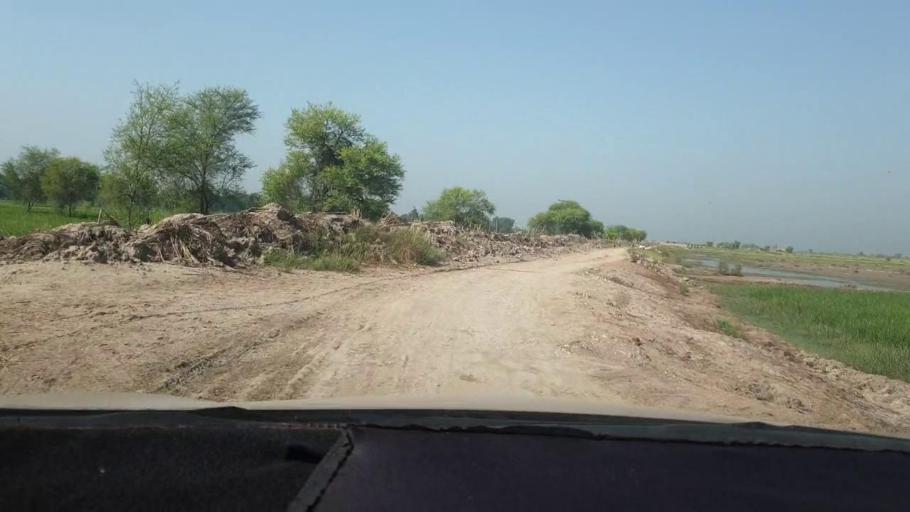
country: PK
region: Sindh
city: Miro Khan
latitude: 27.7177
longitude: 68.1109
